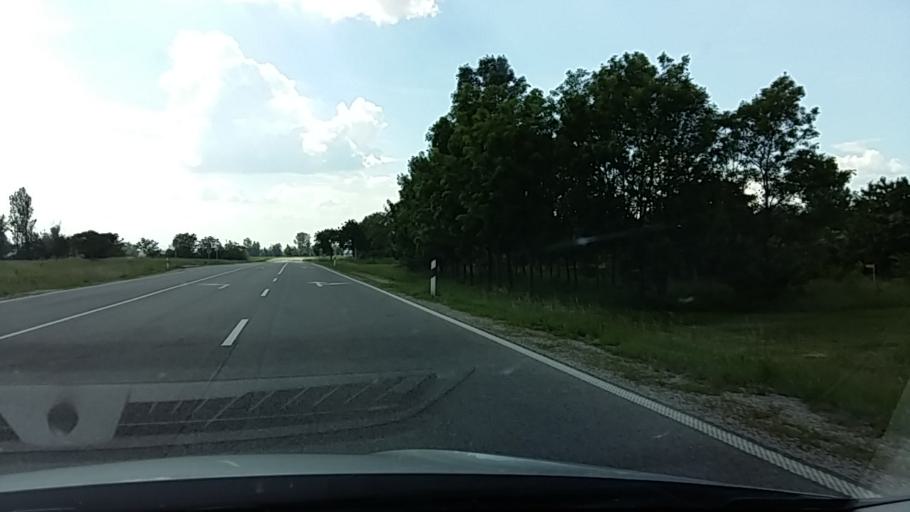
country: HU
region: Gyor-Moson-Sopron
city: Nagycenk
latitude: 47.5970
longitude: 16.7728
